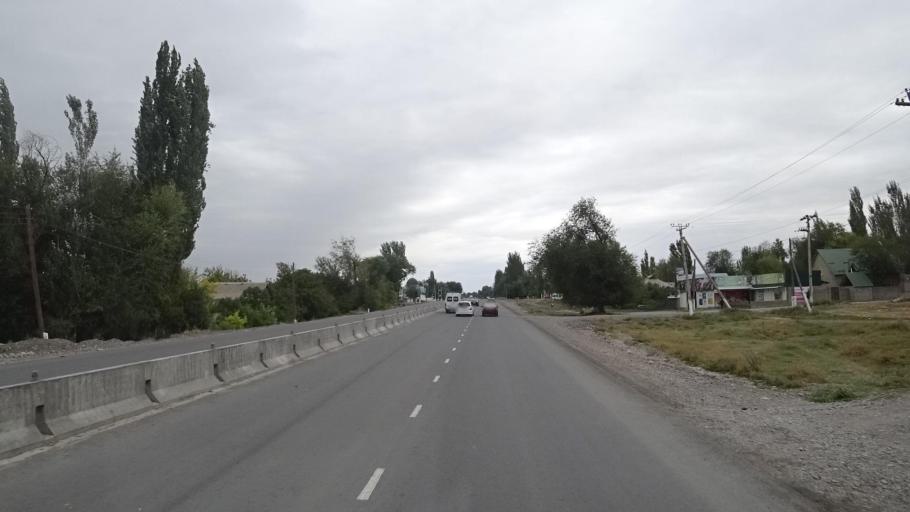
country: KG
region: Chuy
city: Kara-Balta
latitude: 42.8337
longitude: 73.9057
